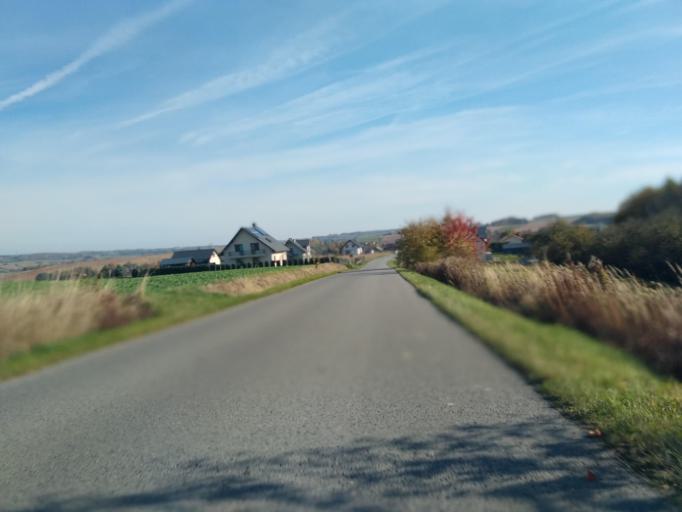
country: PL
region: Subcarpathian Voivodeship
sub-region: Powiat ropczycko-sedziszowski
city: Iwierzyce
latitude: 50.0044
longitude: 21.7453
